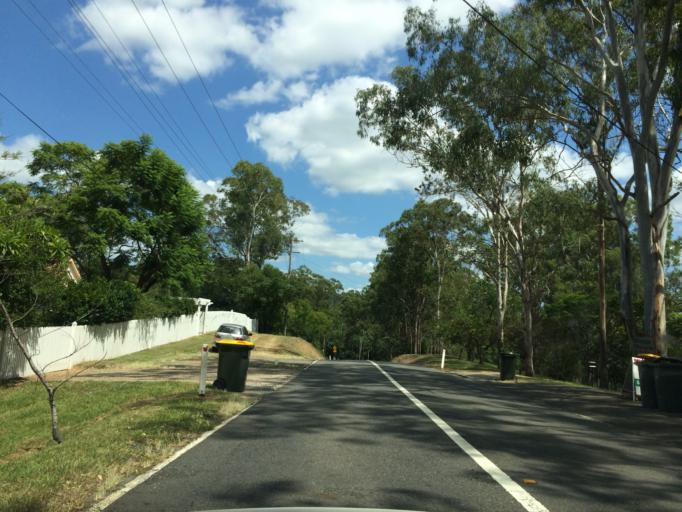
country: AU
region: Queensland
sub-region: Brisbane
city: Kenmore Hills
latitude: -27.4967
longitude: 152.9221
